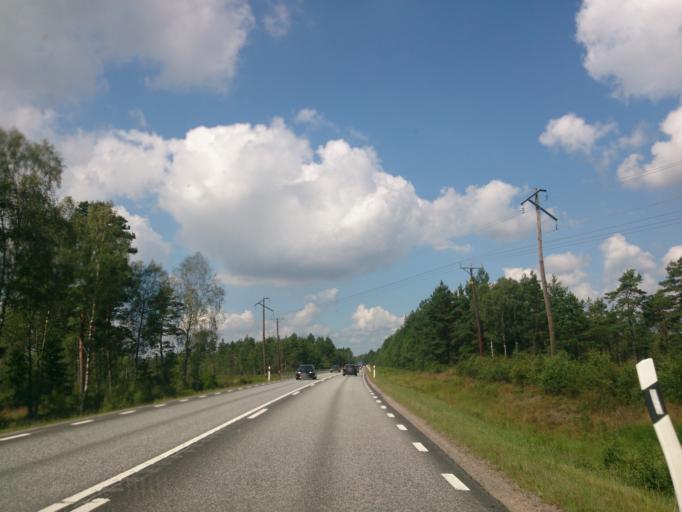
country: SE
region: Joenkoeping
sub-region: Varnamo Kommun
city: Forsheda
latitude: 57.1660
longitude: 13.7914
